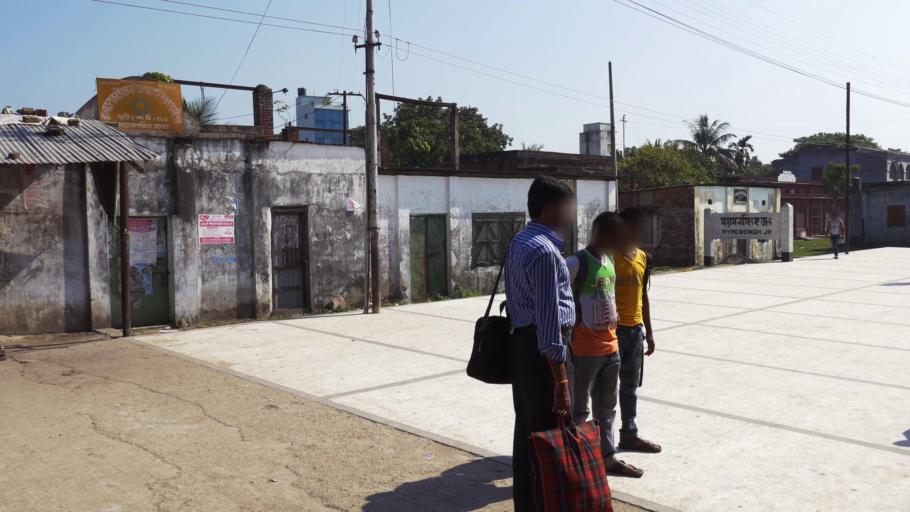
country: BD
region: Dhaka
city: Mymensingh
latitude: 24.6339
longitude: 90.4607
